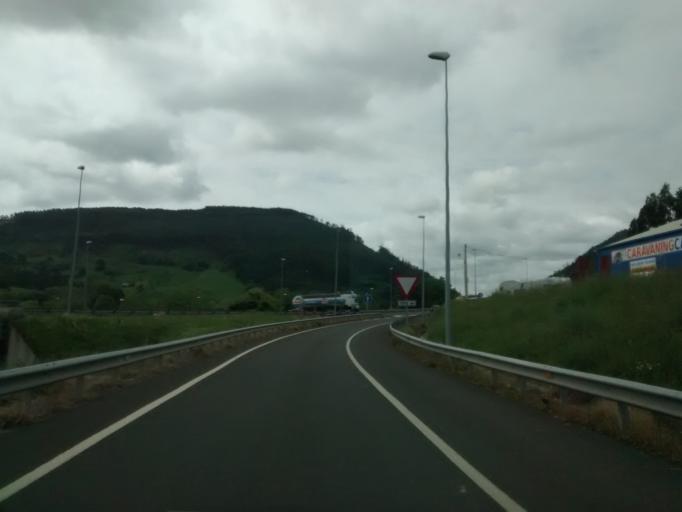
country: ES
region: Cantabria
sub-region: Provincia de Cantabria
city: Cartes
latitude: 43.3179
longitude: -4.0681
